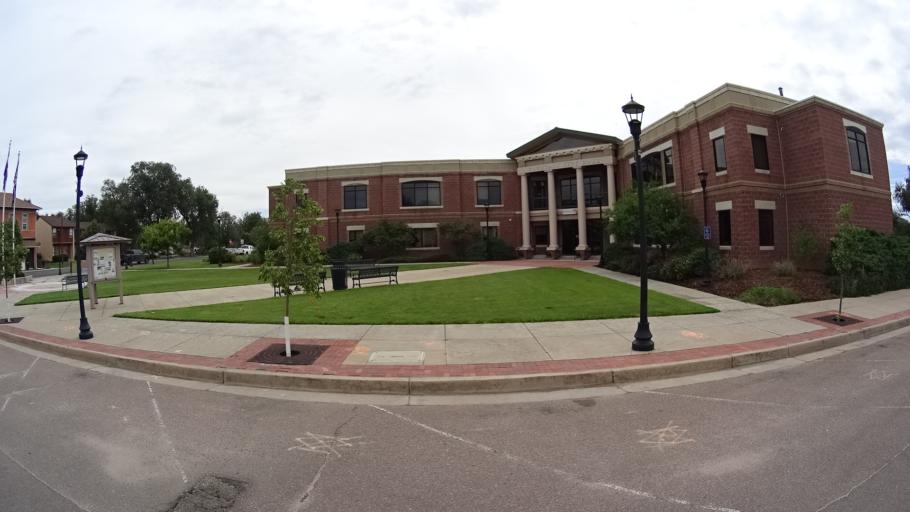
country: US
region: Colorado
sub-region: El Paso County
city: Fountain
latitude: 38.6828
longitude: -104.7007
